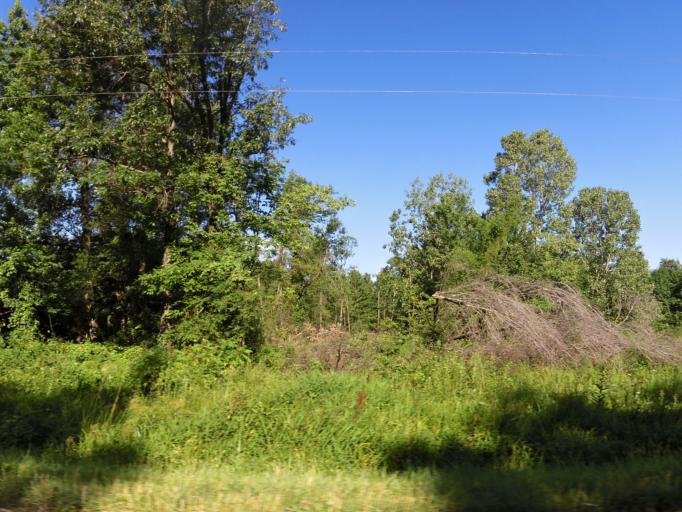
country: US
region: Missouri
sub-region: Butler County
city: Poplar Bluff
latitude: 36.6370
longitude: -90.5203
